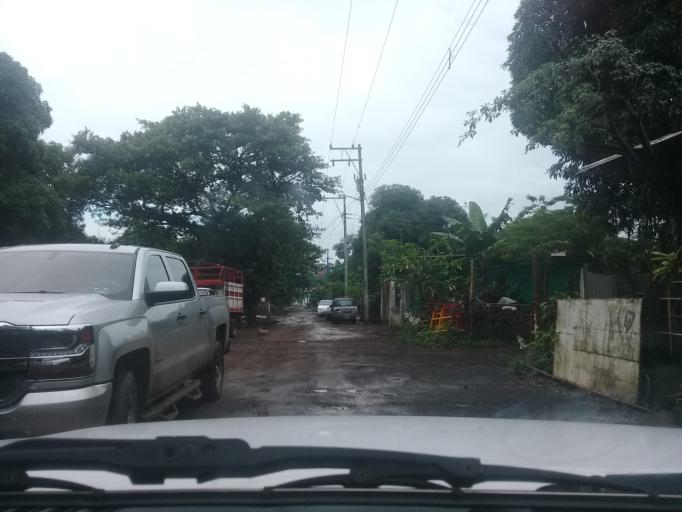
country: MX
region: Veracruz
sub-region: San Andres Tuxtla
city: Cerro las Iguanas
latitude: 18.4281
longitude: -95.1965
